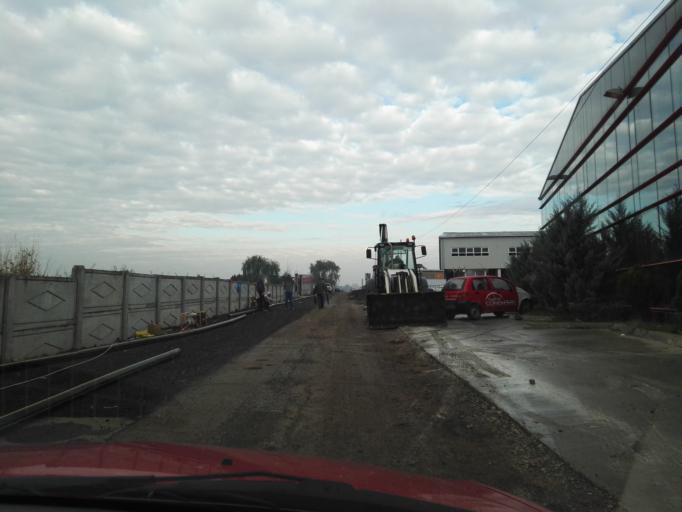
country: RO
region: Ilfov
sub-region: Comuna Magurele
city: Magurele
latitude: 44.3770
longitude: 26.0426
